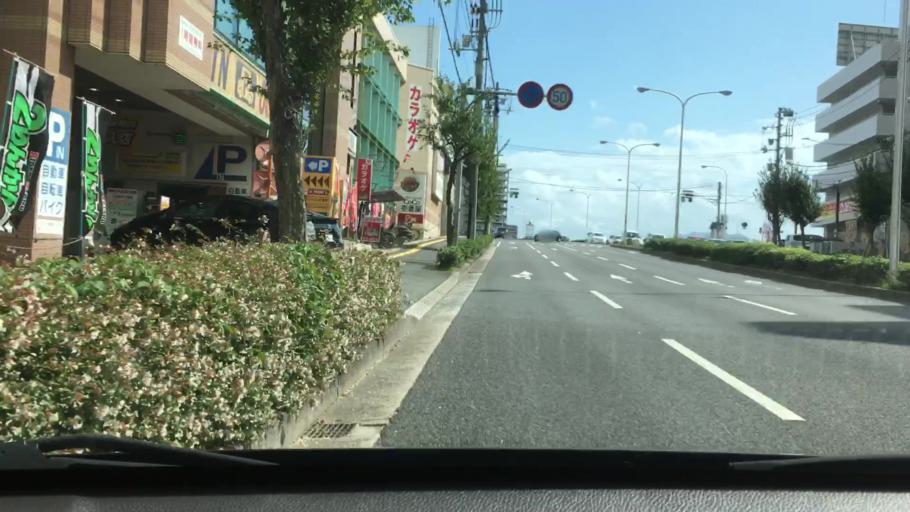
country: JP
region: Hiroshima
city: Hiroshima-shi
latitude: 34.3746
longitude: 132.4402
